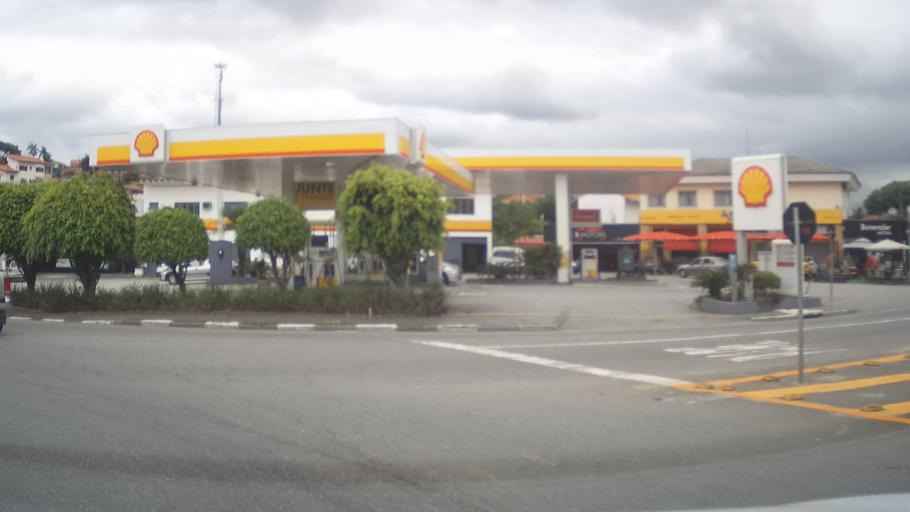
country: BR
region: Sao Paulo
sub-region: Aruja
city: Aruja
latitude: -23.4008
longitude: -46.3188
